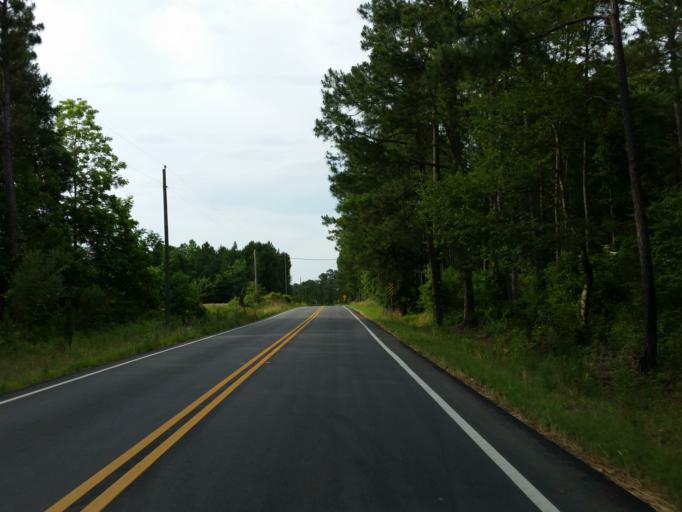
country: US
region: Georgia
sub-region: Turner County
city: Ashburn
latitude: 31.7444
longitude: -83.6677
